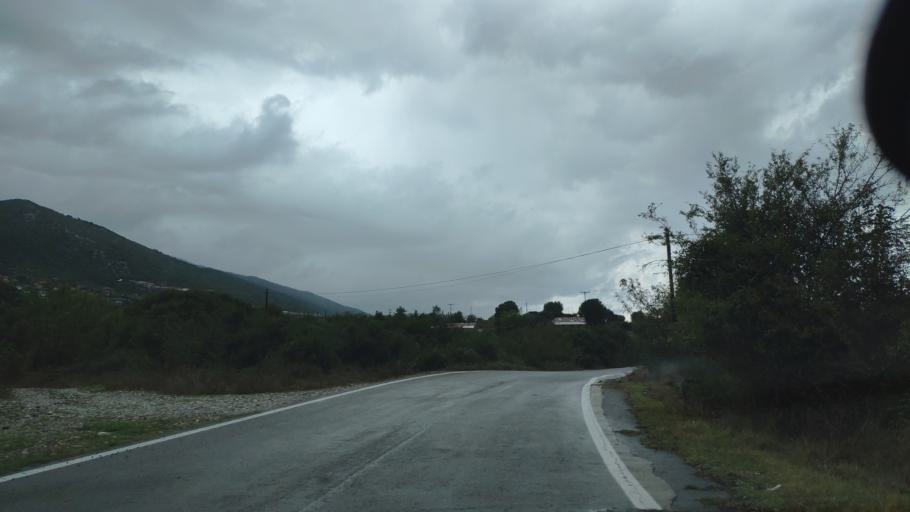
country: GR
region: Central Greece
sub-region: Nomos Evrytanias
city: Kerasochori
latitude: 39.1045
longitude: 21.4232
